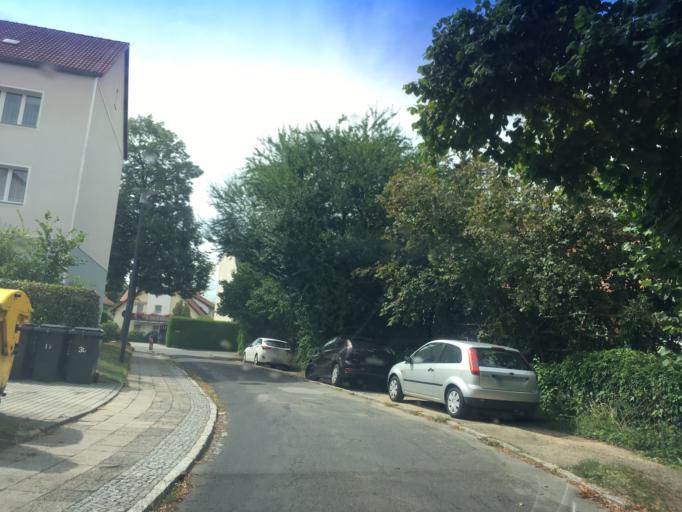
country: DE
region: Saxony
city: Goerlitz
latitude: 51.1462
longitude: 14.9521
